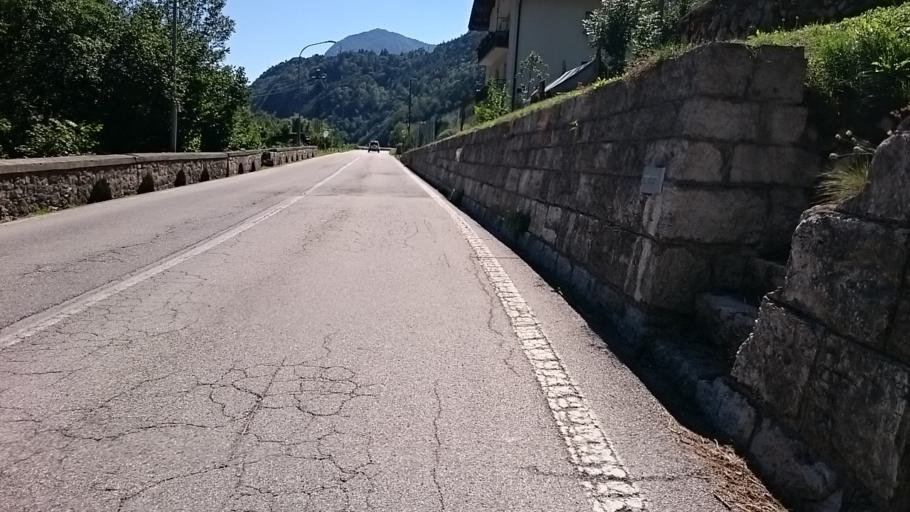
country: IT
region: Veneto
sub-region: Provincia di Belluno
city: Ospitale di Cadore
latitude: 46.3487
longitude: 12.3334
